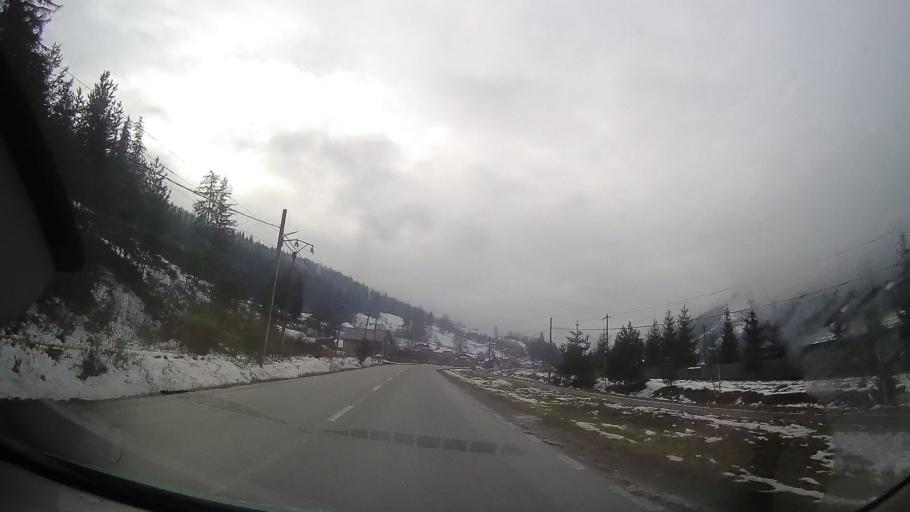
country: RO
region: Neamt
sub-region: Comuna Tasca
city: Tasca
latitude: 46.8900
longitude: 26.0153
